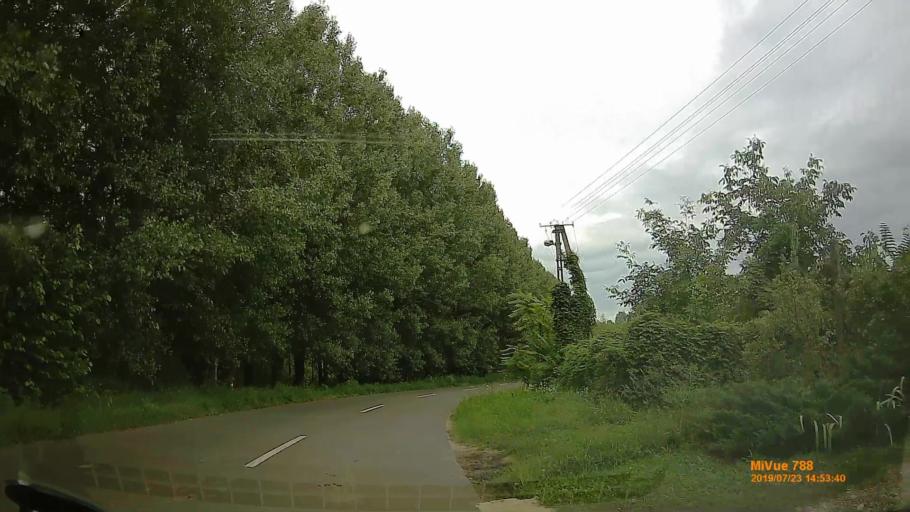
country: HU
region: Szabolcs-Szatmar-Bereg
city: Kalmanhaza
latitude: 47.8801
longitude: 21.6520
